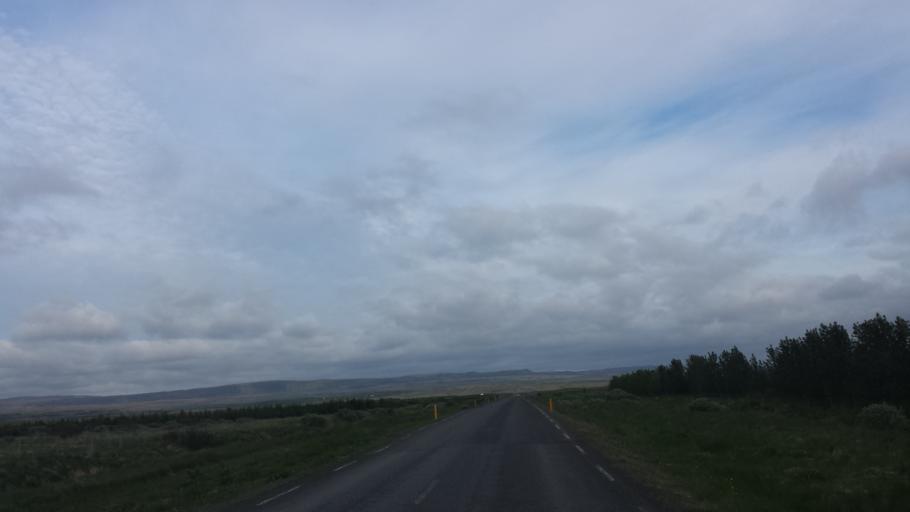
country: IS
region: South
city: Selfoss
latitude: 64.2644
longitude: -20.3437
